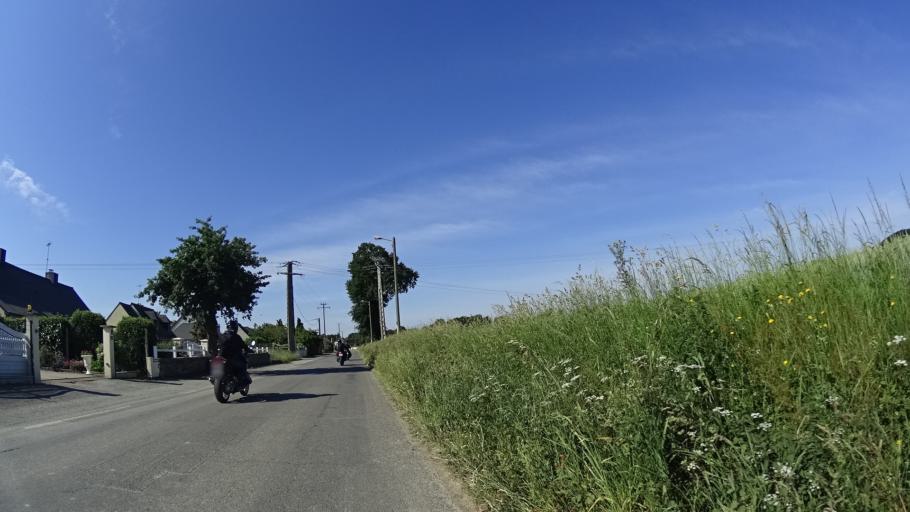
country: FR
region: Brittany
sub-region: Departement d'Ille-et-Vilaine
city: Guipry
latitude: 47.8190
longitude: -1.8468
